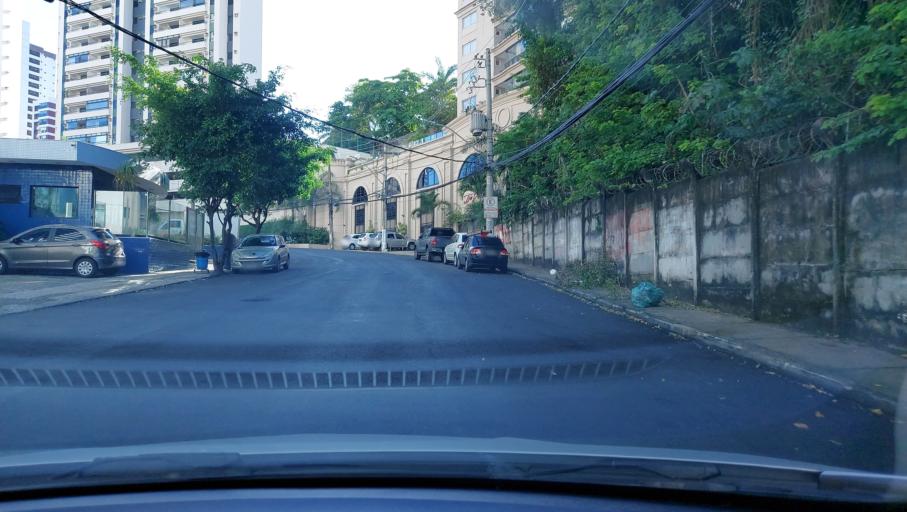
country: BR
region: Bahia
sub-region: Salvador
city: Salvador
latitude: -12.9859
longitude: -38.4535
